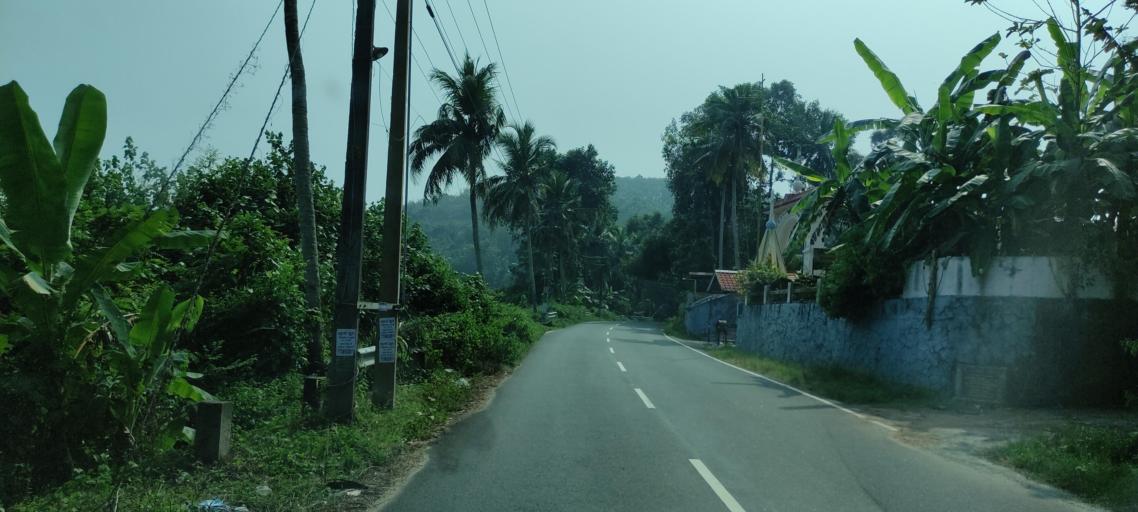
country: IN
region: Kerala
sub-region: Pattanamtitta
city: Adur
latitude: 9.2340
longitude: 76.6975
